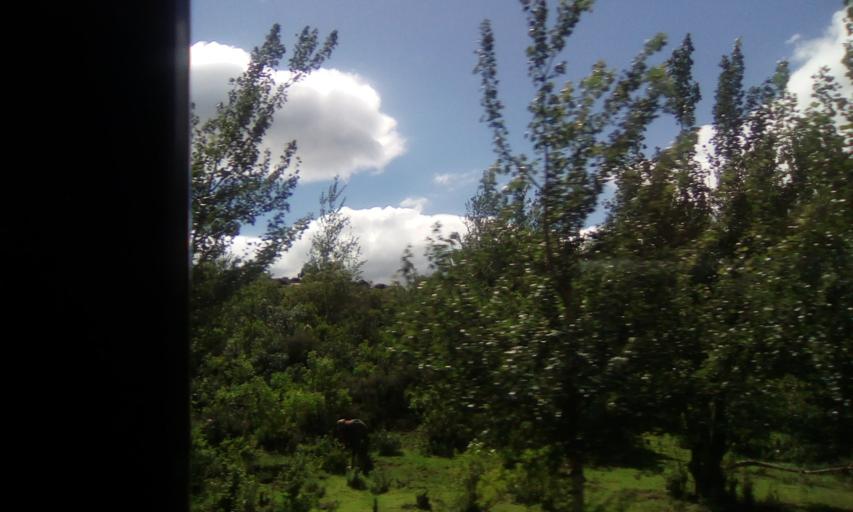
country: LS
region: Maseru
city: Nako
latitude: -29.6590
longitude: 27.8075
